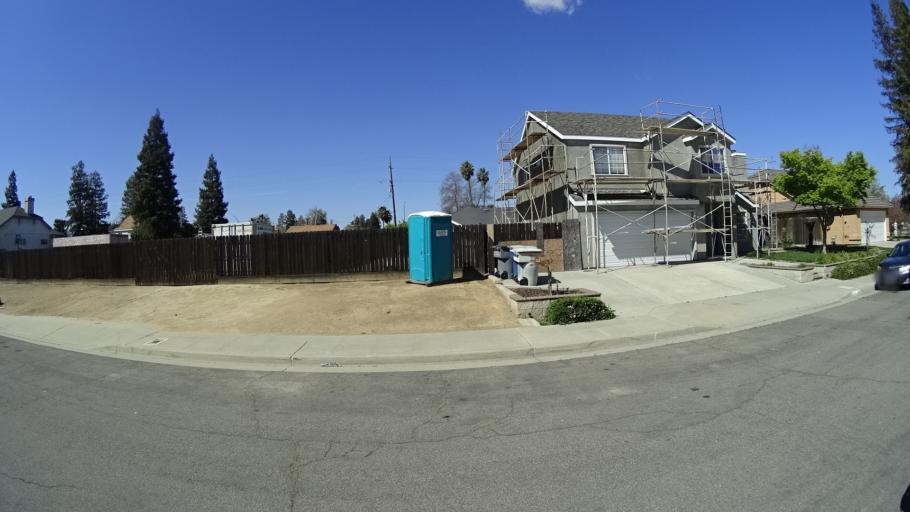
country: US
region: California
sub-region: Fresno County
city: West Park
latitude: 36.7913
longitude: -119.8793
